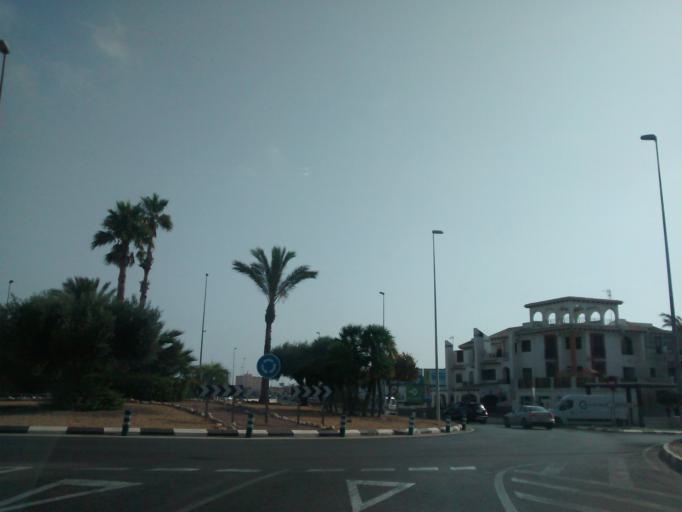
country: ES
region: Valencia
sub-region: Provincia de Alicante
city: Pilar de la Horadada
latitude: 37.9152
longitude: -0.7363
